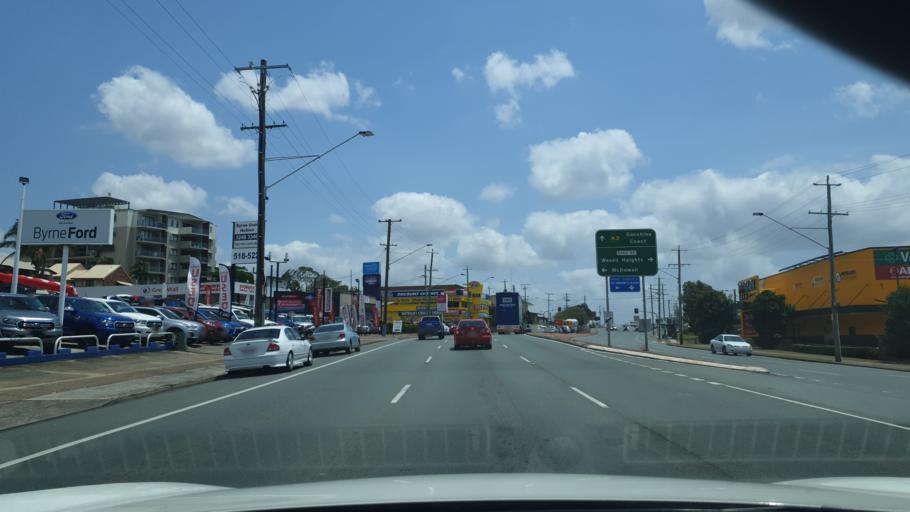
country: AU
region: Queensland
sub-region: Brisbane
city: Wavell Heights
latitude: -27.3954
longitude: 153.0308
